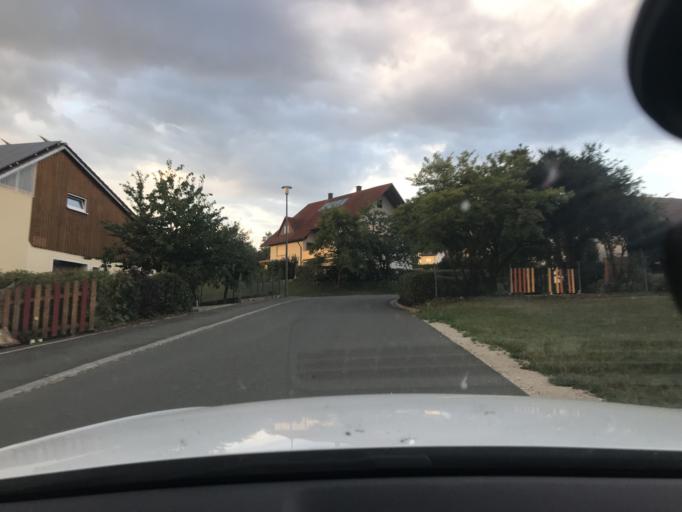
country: DE
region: Bavaria
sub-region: Upper Palatinate
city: Auerbach
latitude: 49.7211
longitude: 11.6185
